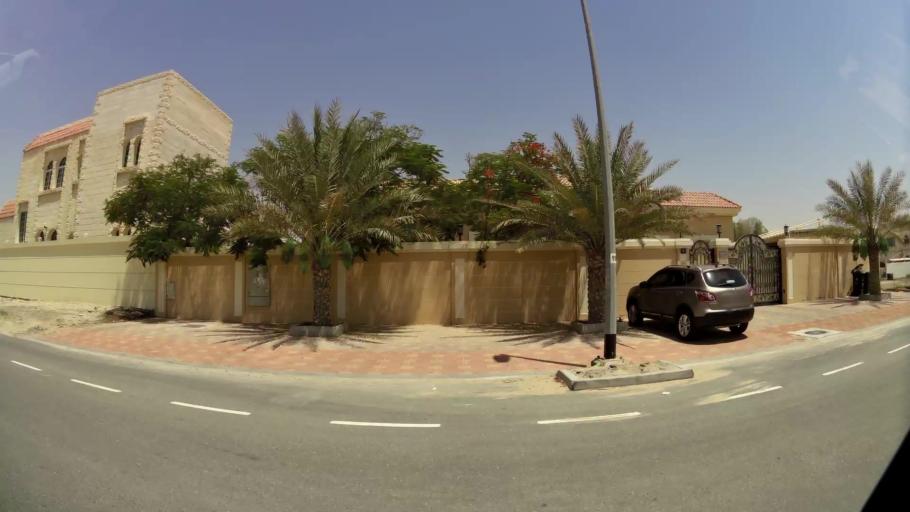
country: AE
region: Dubai
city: Dubai
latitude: 25.0875
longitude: 55.2105
